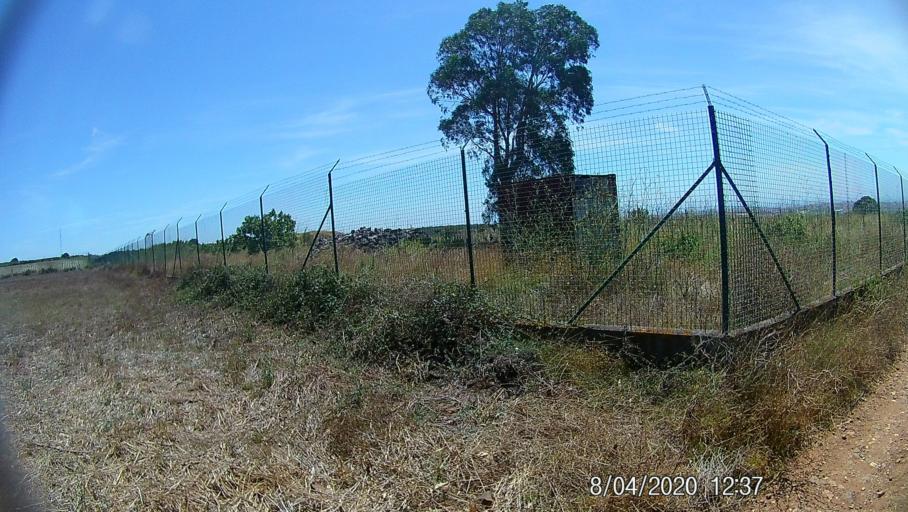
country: PT
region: Lisbon
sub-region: Sintra
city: Rio de Mouro
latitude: 38.7473
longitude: -9.3641
